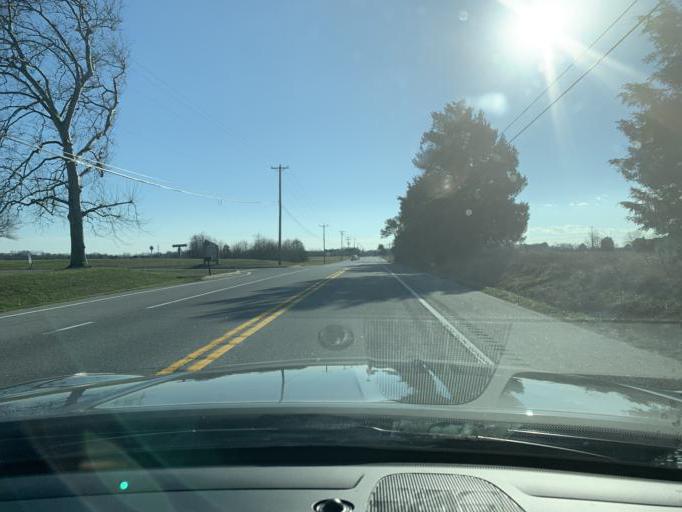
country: US
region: Maryland
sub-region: Queen Anne's County
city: Centreville
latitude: 39.0699
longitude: -76.0489
